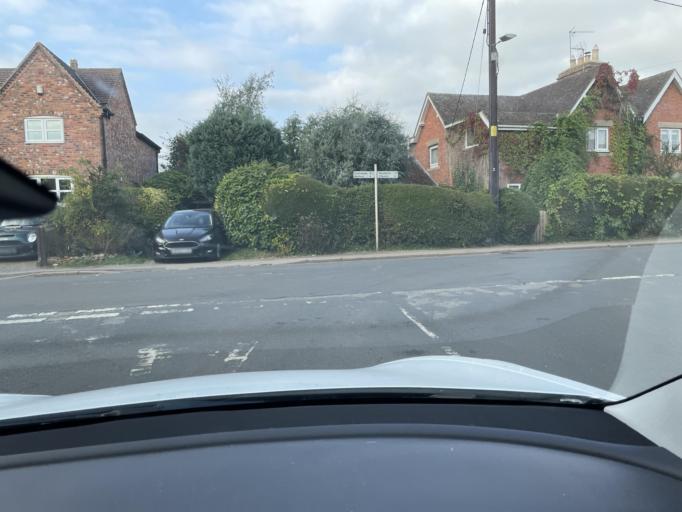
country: GB
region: England
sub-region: Leicestershire
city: Market Harborough
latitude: 52.3969
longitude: -0.9868
